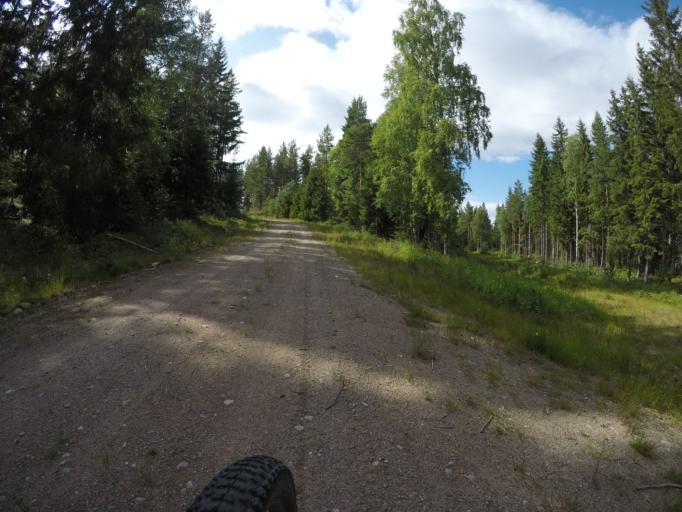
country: SE
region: Dalarna
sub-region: Ludvika Kommun
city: Abborrberget
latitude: 60.0508
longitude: 14.5877
